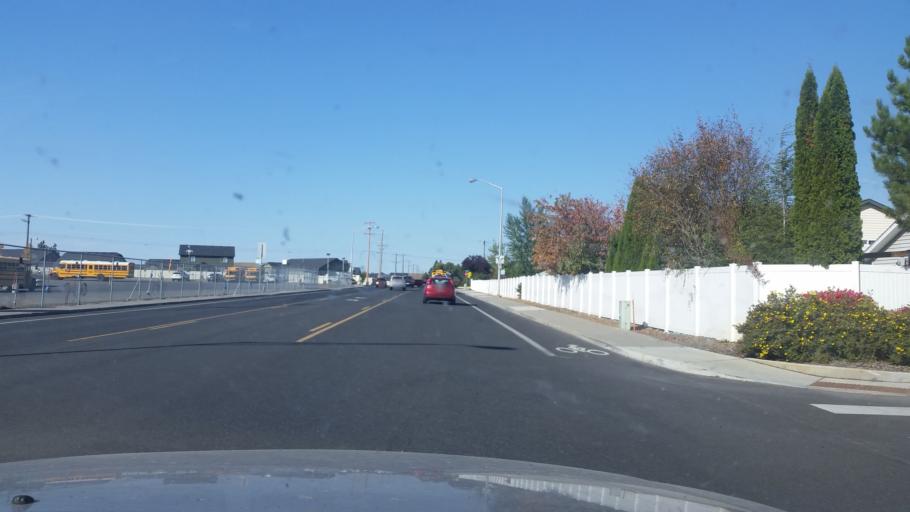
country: US
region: Washington
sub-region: Spokane County
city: Cheney
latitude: 47.5060
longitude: -117.5755
